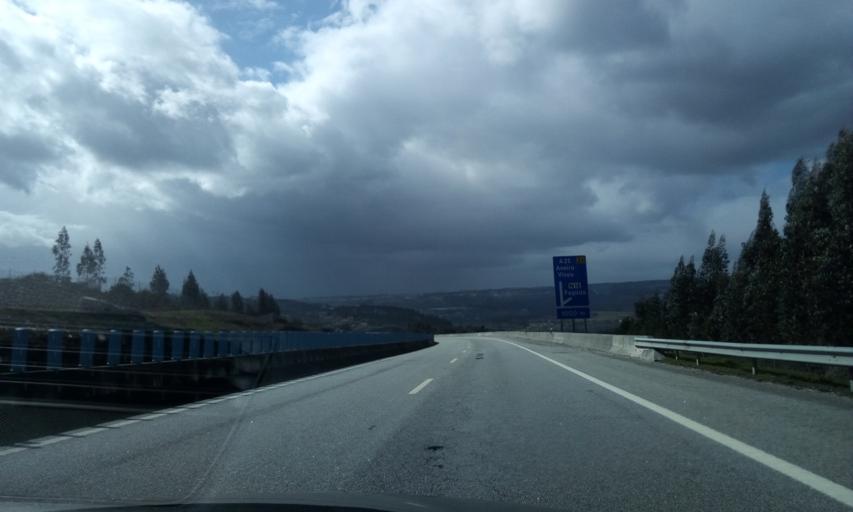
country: PT
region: Viseu
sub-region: Mangualde
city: Mangualde
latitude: 40.6277
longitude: -7.7876
